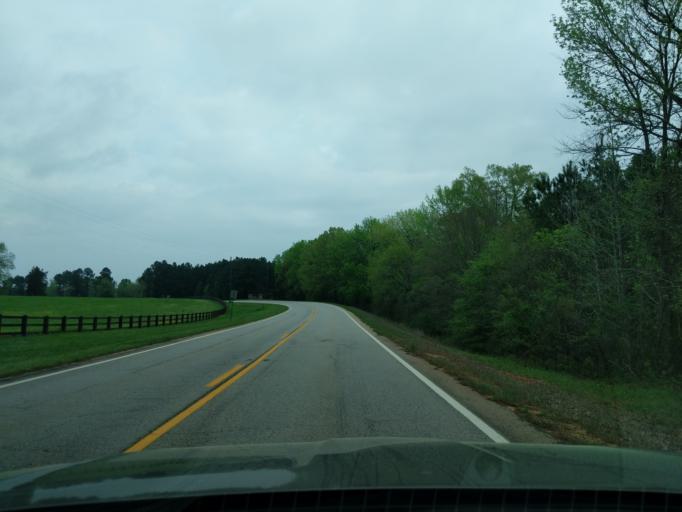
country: US
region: Georgia
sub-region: Lincoln County
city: Lincolnton
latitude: 33.7885
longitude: -82.3802
